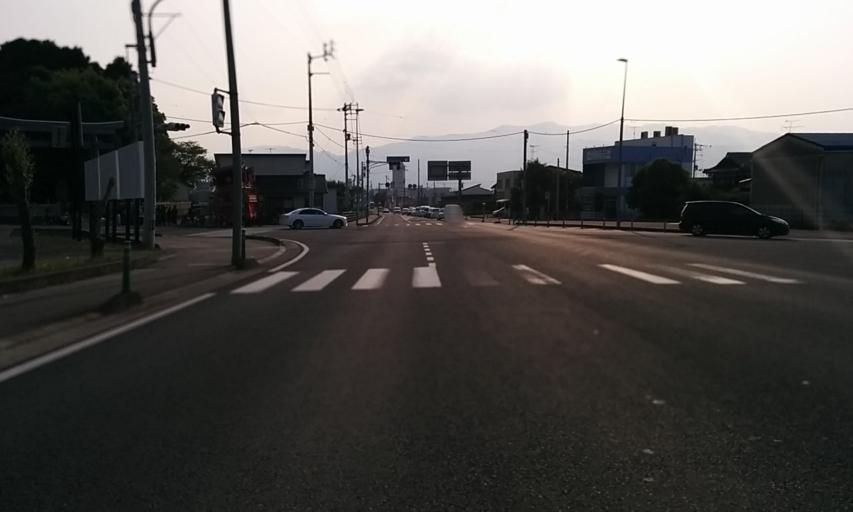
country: JP
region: Ehime
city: Saijo
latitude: 33.8972
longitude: 133.1090
